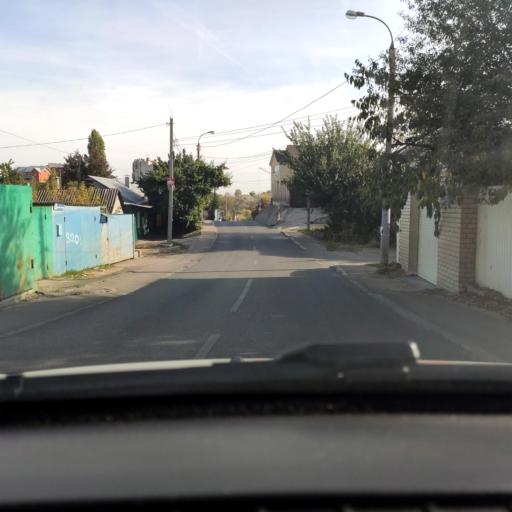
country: RU
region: Voronezj
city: Voronezh
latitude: 51.6563
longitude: 39.1978
